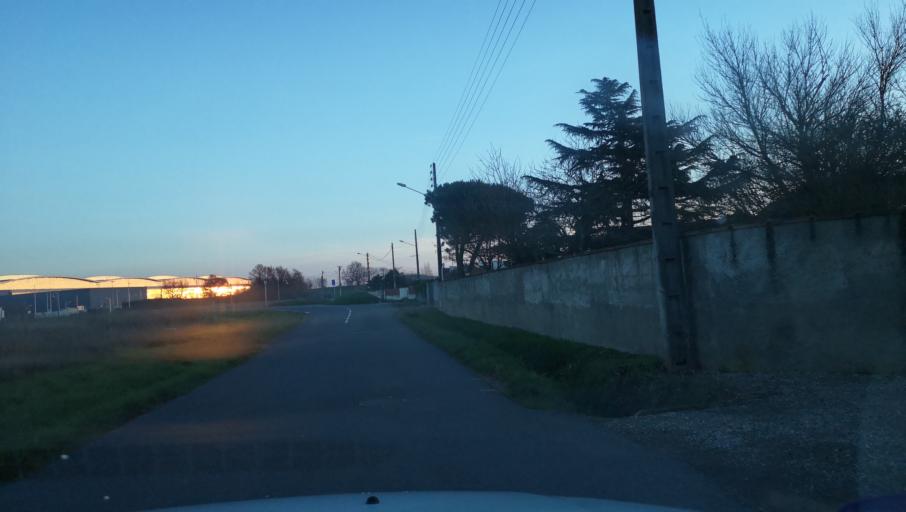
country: FR
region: Midi-Pyrenees
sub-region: Departement de la Haute-Garonne
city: Cornebarrieu
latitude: 43.6624
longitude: 1.3457
